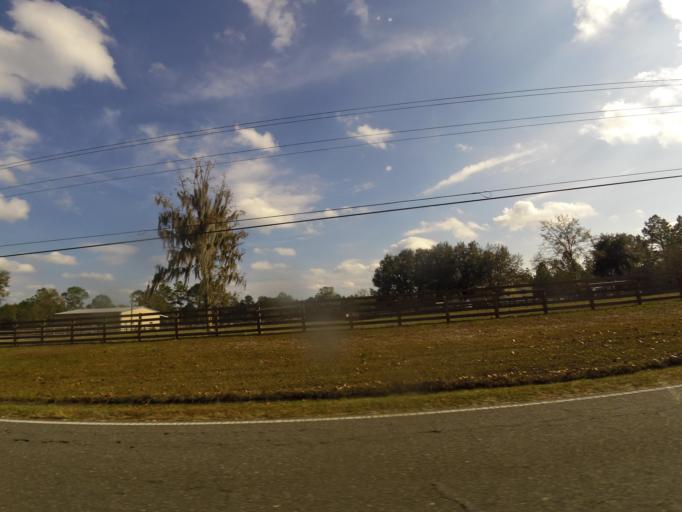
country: US
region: Florida
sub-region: Duval County
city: Baldwin
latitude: 30.1770
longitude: -81.9925
